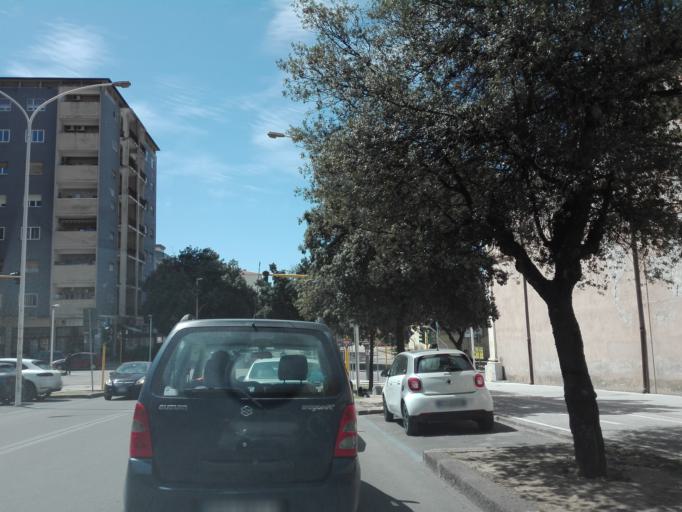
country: IT
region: Sardinia
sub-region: Provincia di Sassari
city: Sassari
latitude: 40.7212
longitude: 8.5650
